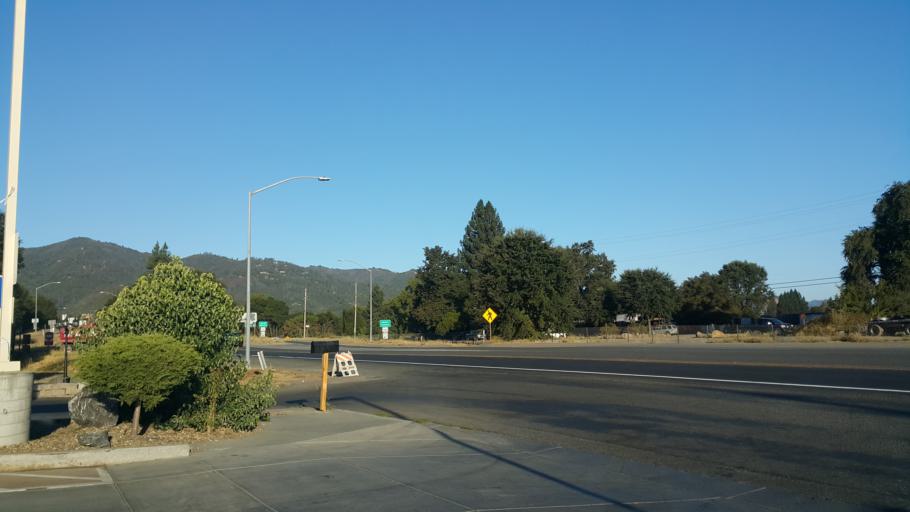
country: US
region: California
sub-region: Mendocino County
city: Ukiah
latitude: 39.1359
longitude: -123.1927
